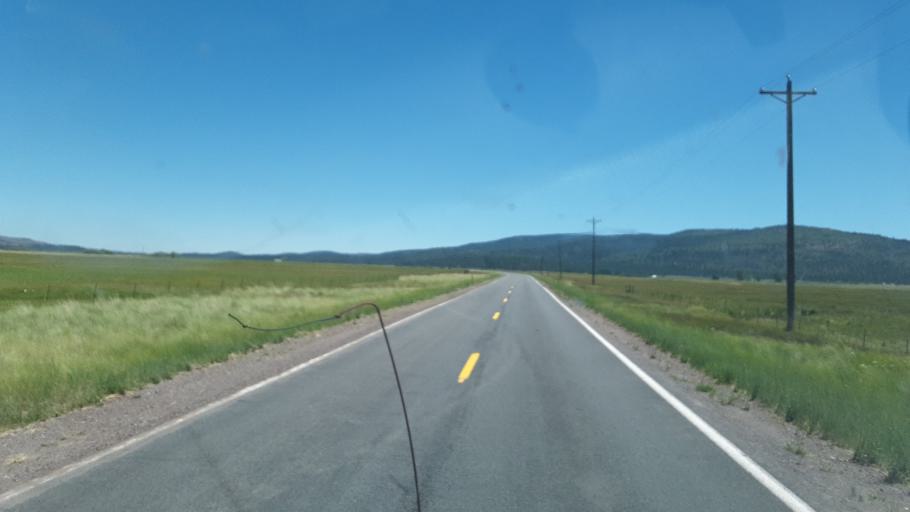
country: US
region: California
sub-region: Lassen County
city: Susanville
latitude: 40.5609
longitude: -120.6392
